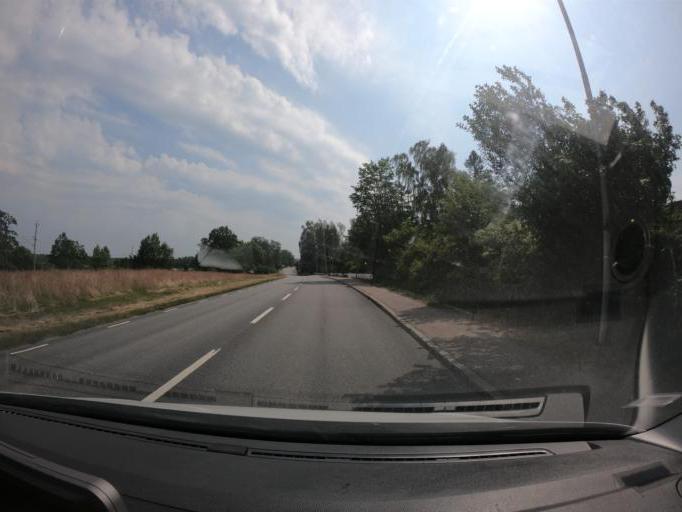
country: SE
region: Skane
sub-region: Hassleholms Kommun
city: Bjarnum
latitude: 56.3496
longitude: 13.6618
